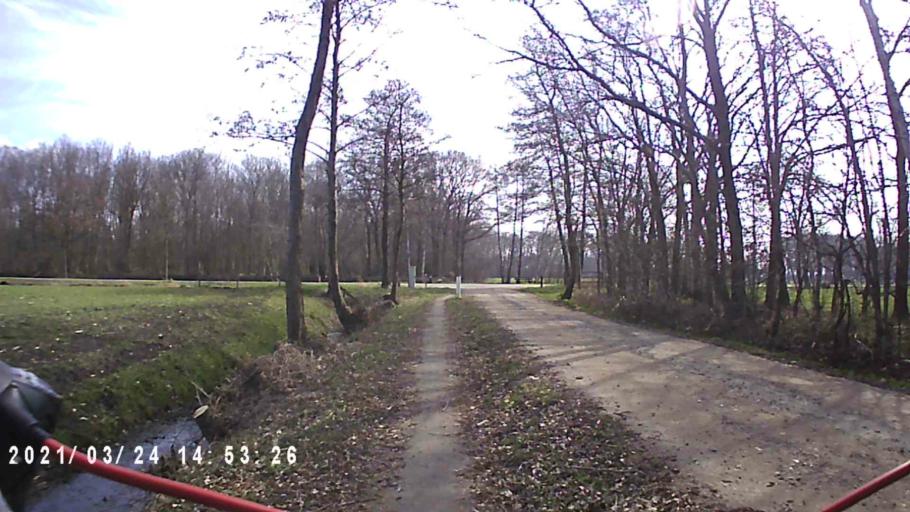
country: NL
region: Friesland
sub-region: Gemeente Heerenveen
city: Jubbega
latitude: 53.0259
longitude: 6.1051
